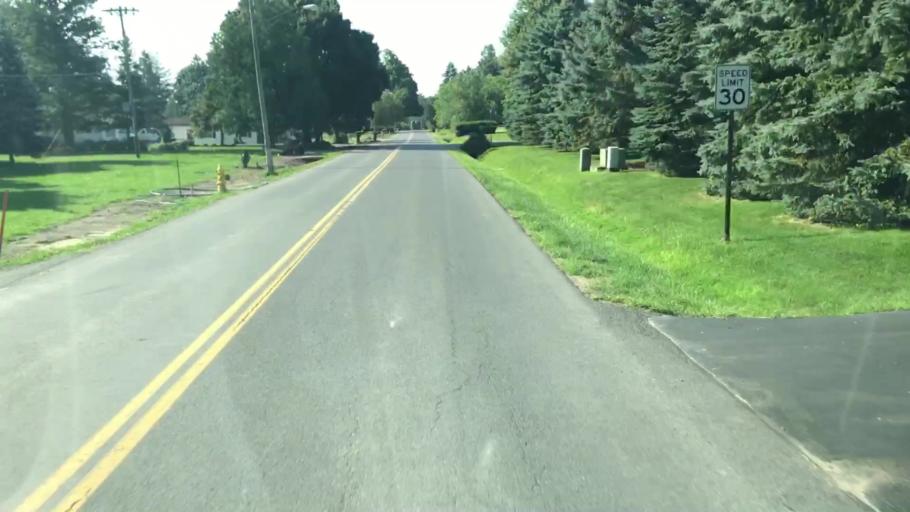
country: US
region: New York
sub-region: Cayuga County
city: Melrose Park
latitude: 42.9111
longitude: -76.5294
